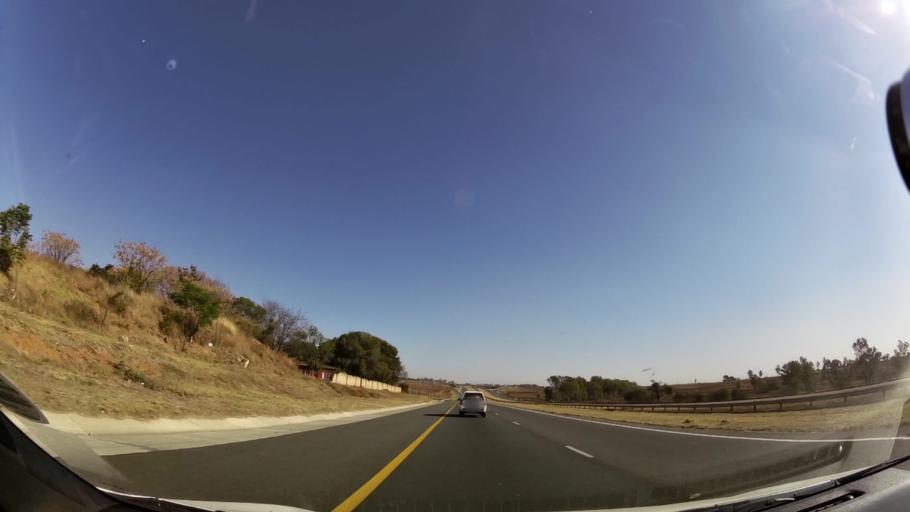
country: ZA
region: Gauteng
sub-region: City of Johannesburg Metropolitan Municipality
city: Diepsloot
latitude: -25.9780
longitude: 27.9337
